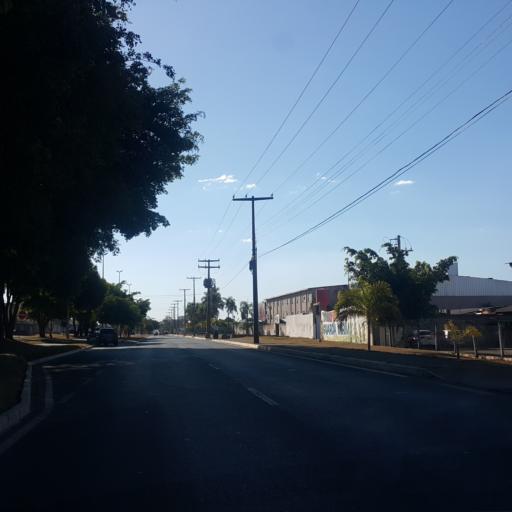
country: BR
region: Federal District
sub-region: Brasilia
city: Brasilia
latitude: -15.8101
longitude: -48.1004
